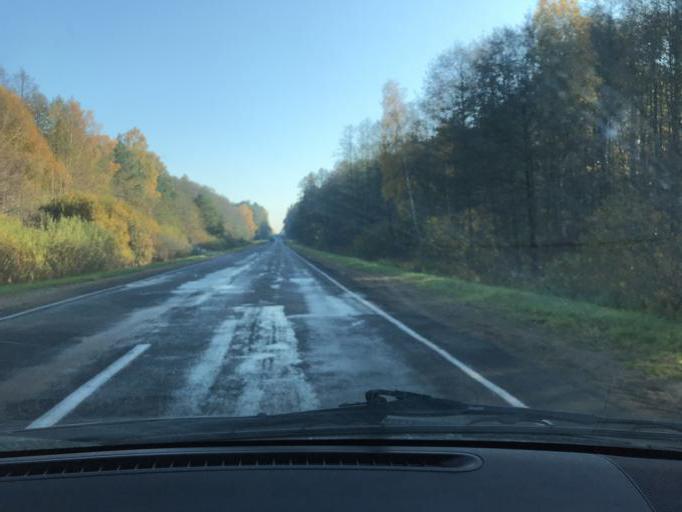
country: BY
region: Brest
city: Lyakhavichy
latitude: 52.9541
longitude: 26.2507
